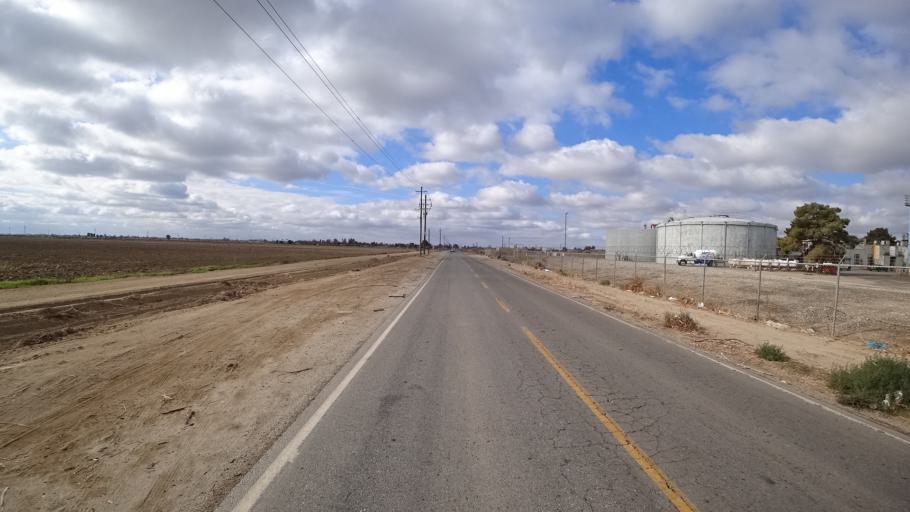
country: US
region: California
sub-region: Kern County
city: Greenfield
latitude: 35.3250
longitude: -118.9725
